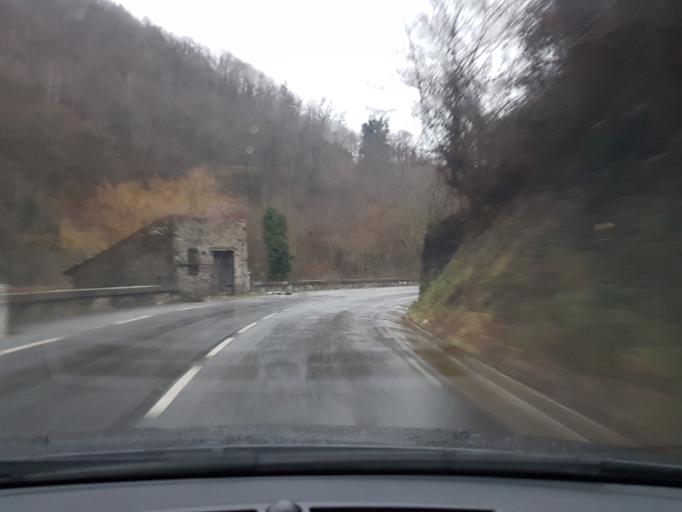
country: FR
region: Midi-Pyrenees
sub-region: Departement de l'Ariege
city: Saint-Girons
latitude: 42.9412
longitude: 1.1766
